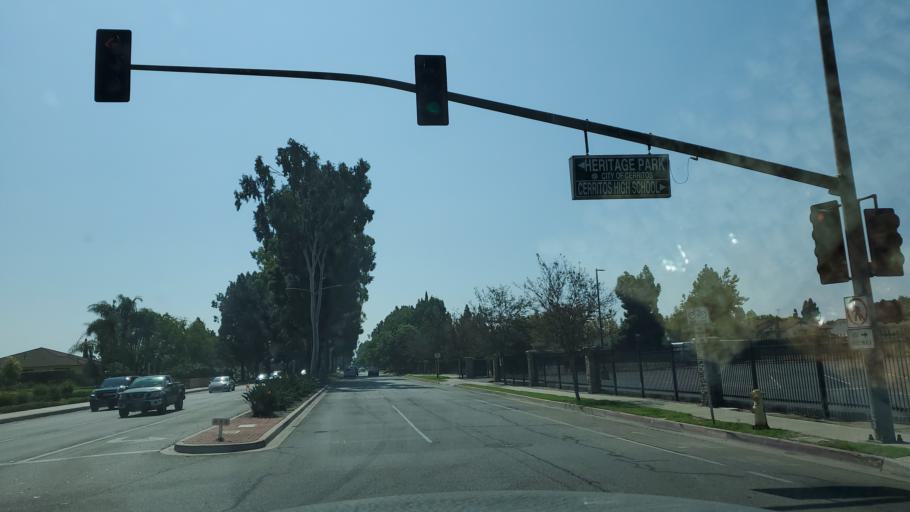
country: US
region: California
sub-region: Los Angeles County
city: Cerritos
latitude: 33.8634
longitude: -118.0638
